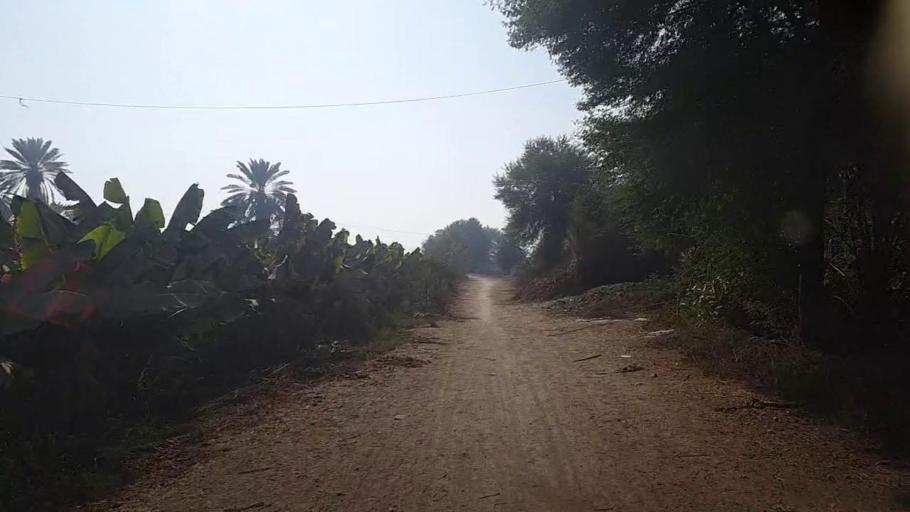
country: PK
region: Sindh
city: Kandiari
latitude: 27.0145
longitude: 68.5018
